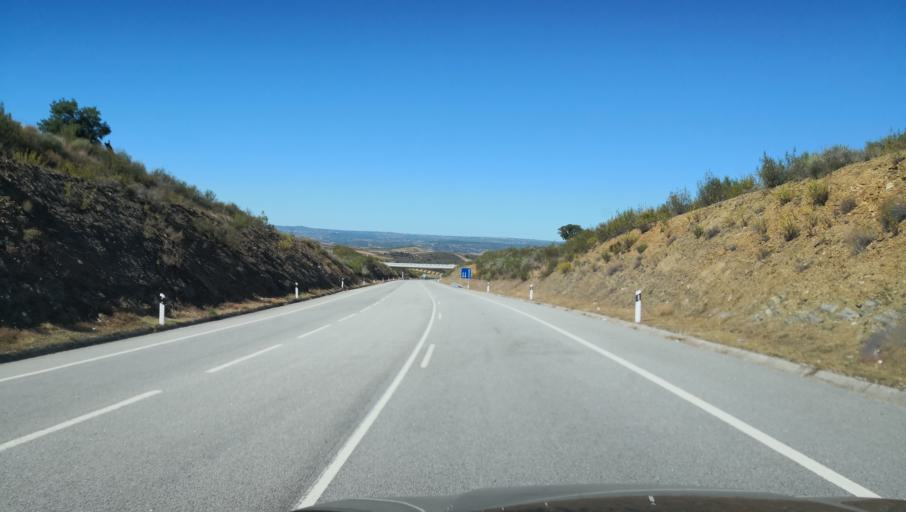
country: PT
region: Braganca
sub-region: Mirandela
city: Mirandela
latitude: 41.4893
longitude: -7.2243
